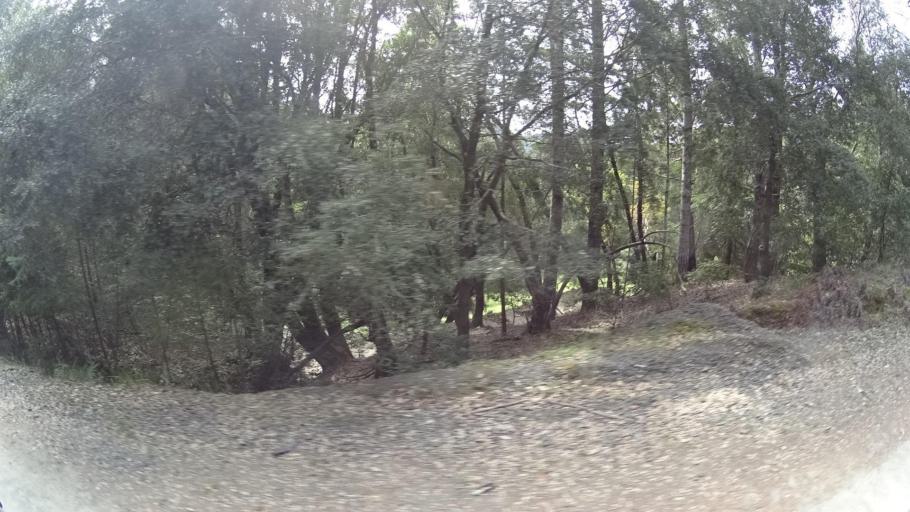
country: US
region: California
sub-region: Humboldt County
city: Redway
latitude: 40.0395
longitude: -123.8454
